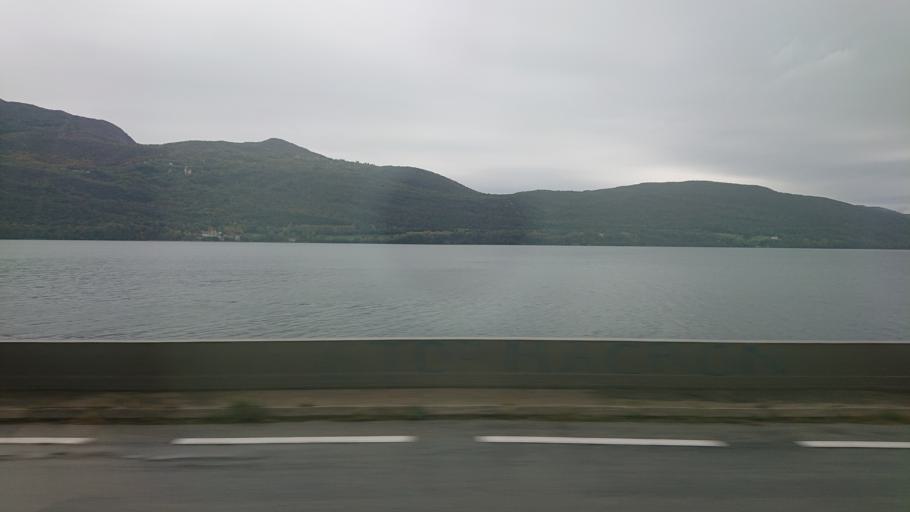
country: FR
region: Rhone-Alpes
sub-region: Departement de la Savoie
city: Brison-Saint-Innocent
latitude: 45.7630
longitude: 5.8703
